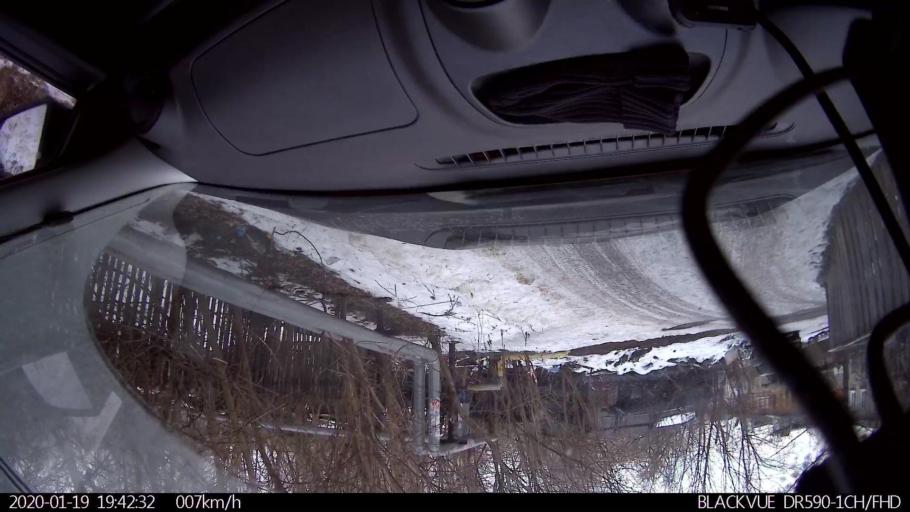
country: RU
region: Nizjnij Novgorod
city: Nizhniy Novgorod
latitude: 56.3010
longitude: 43.9093
